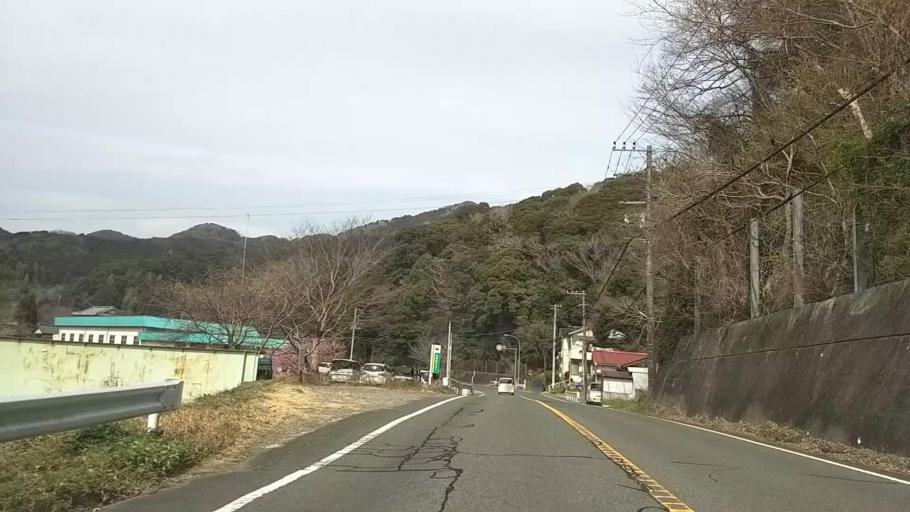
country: JP
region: Shizuoka
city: Shimoda
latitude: 34.7209
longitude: 138.9464
